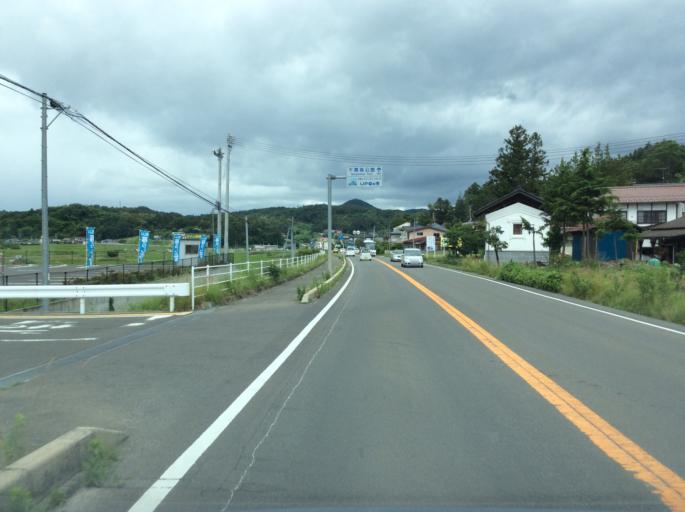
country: JP
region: Fukushima
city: Fukushima-shi
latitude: 37.6693
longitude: 140.5738
